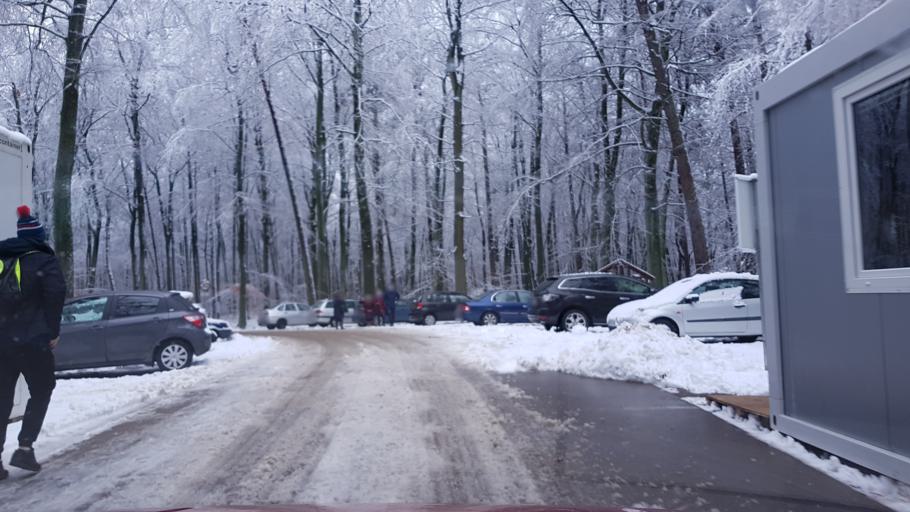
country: PL
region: West Pomeranian Voivodeship
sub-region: Powiat drawski
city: Zlocieniec
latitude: 53.5044
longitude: 15.9878
